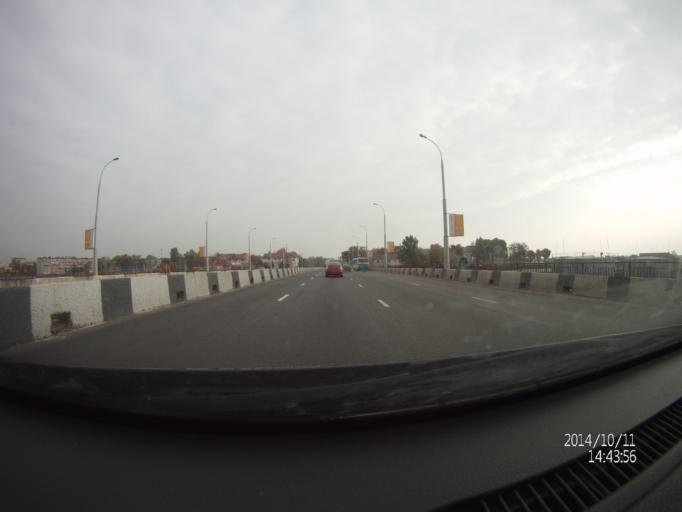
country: BY
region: Minsk
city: Syenitsa
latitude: 53.8751
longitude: 27.5242
